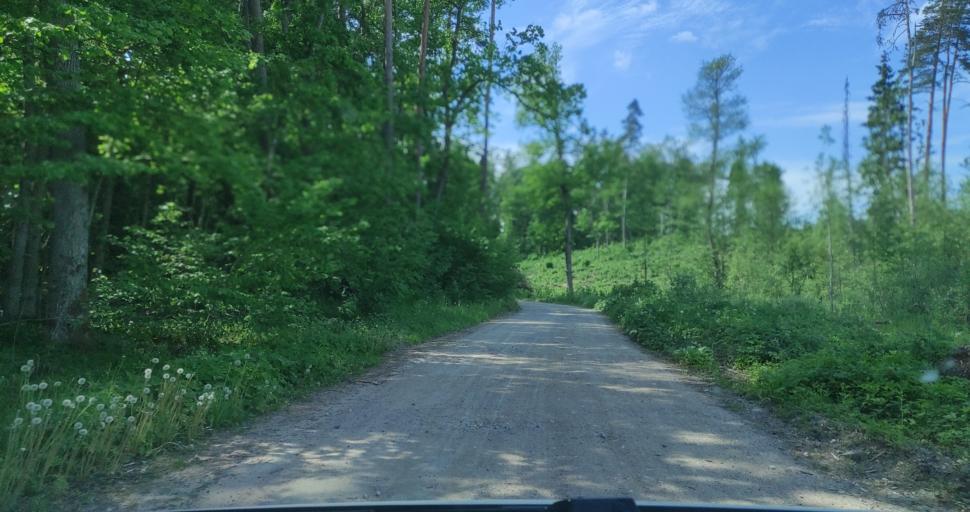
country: LV
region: Kuldigas Rajons
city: Kuldiga
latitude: 56.8498
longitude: 21.9186
